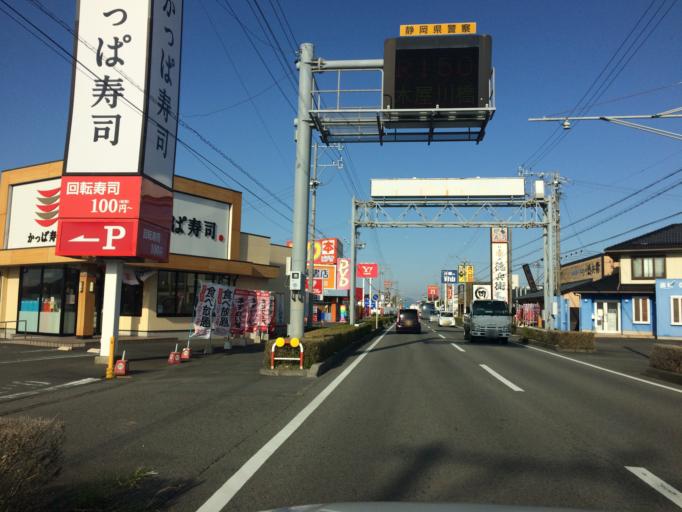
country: JP
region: Shizuoka
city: Shimada
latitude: 34.7606
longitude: 138.2457
